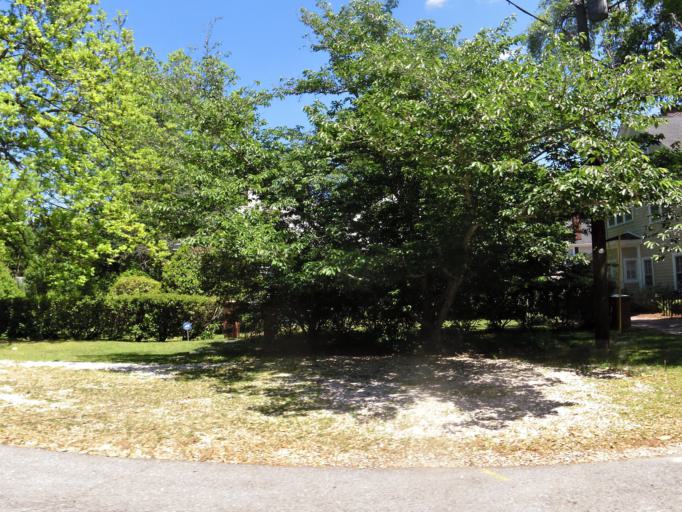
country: US
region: South Carolina
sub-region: Aiken County
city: Aiken
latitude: 33.5564
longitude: -81.7164
